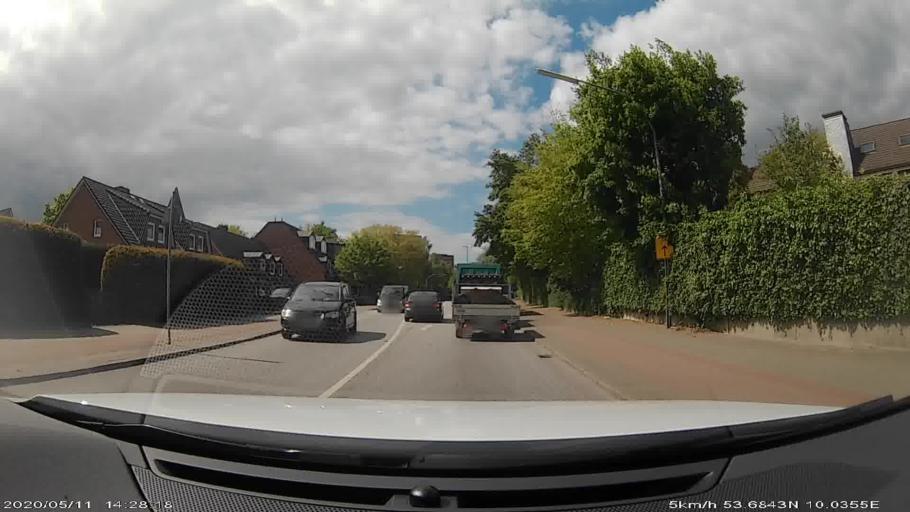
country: DE
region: Hamburg
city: Hummelsbuettel
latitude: 53.6822
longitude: 10.0330
